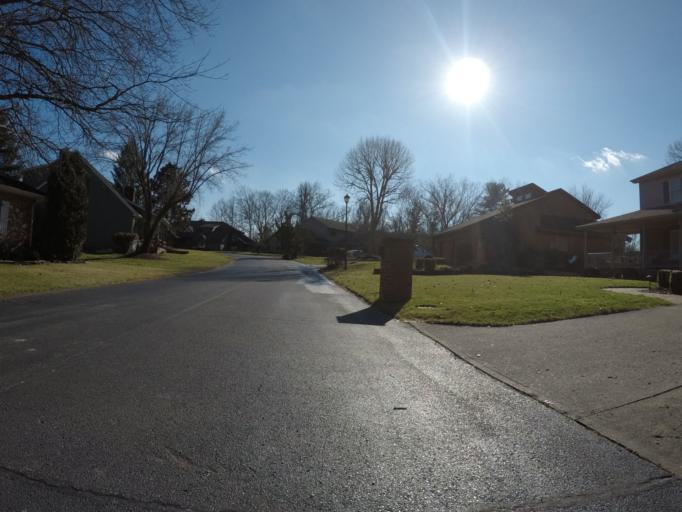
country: US
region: West Virginia
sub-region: Cabell County
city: Pea Ridge
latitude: 38.4207
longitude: -82.3286
